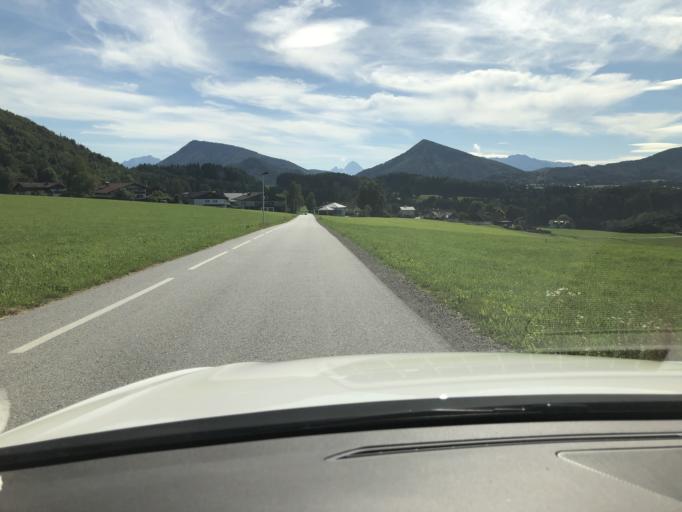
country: AT
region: Salzburg
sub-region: Politischer Bezirk Salzburg-Umgebung
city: Plainfeld
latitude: 47.8216
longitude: 13.1865
